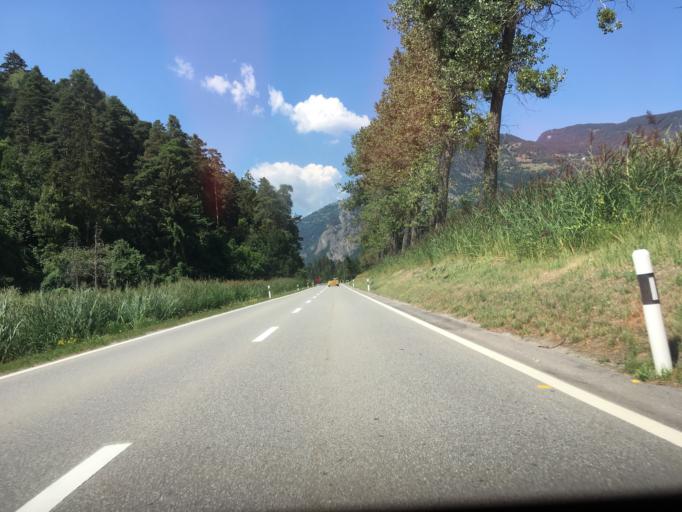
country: CH
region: Grisons
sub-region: Hinterrhein District
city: Cazis
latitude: 46.7434
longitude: 9.4263
